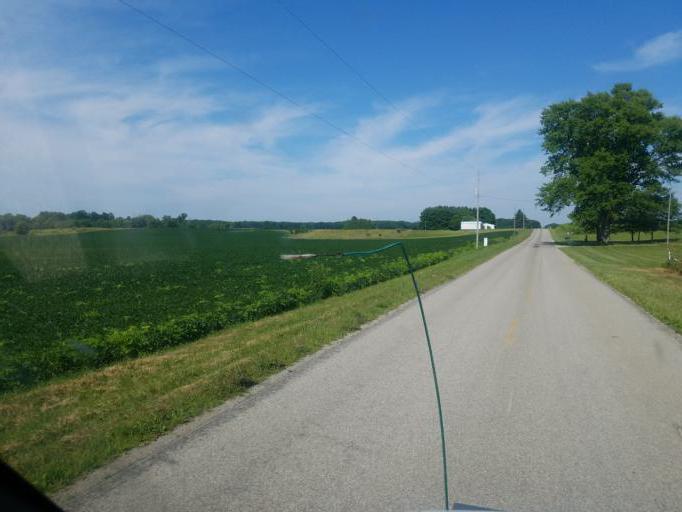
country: US
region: Ohio
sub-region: Hardin County
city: Kenton
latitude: 40.5548
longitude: -83.6428
